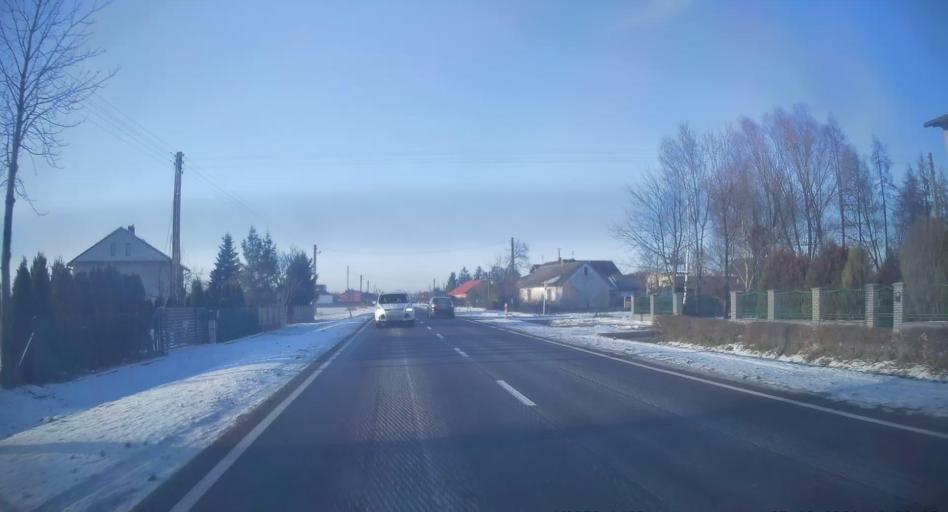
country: PL
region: Lodz Voivodeship
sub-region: Powiat opoczynski
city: Mniszkow
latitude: 51.3254
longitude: 20.0422
